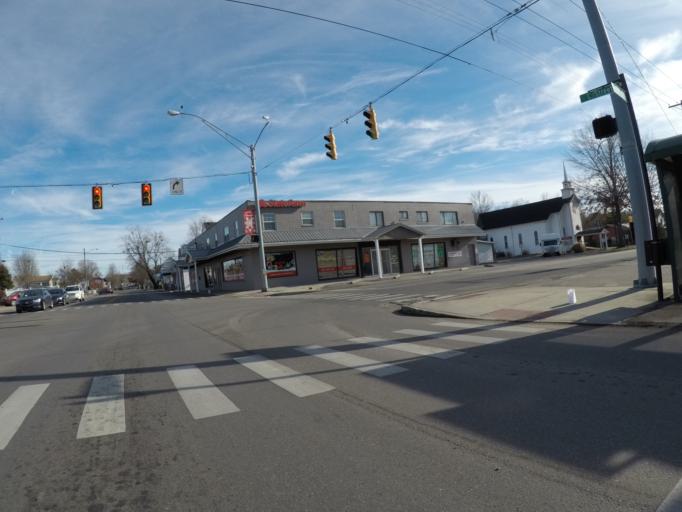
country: US
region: West Virginia
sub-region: Wayne County
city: Ceredo
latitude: 38.3965
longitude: -82.5589
